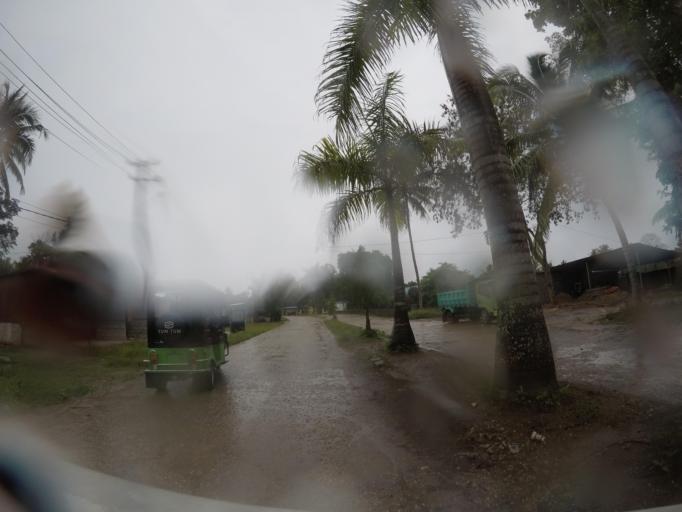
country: TL
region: Lautem
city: Lospalos
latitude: -8.5138
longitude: 127.0034
